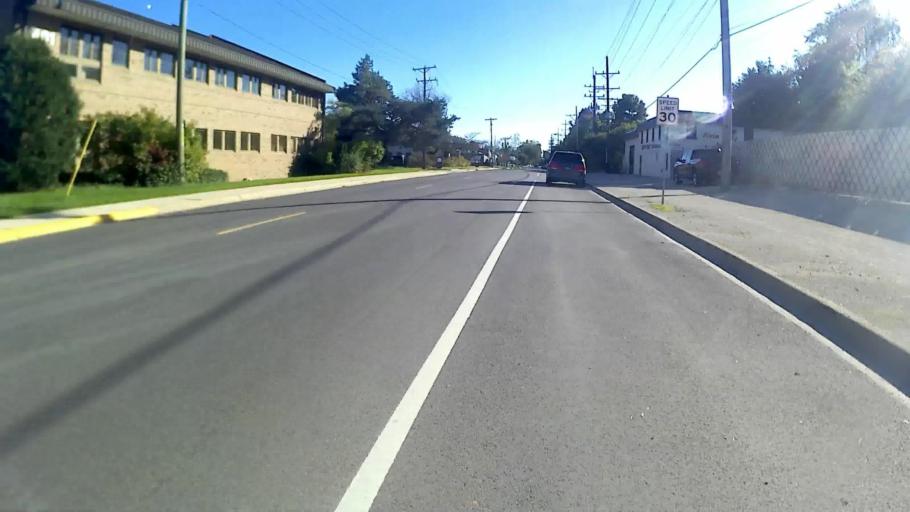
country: US
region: Illinois
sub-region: DuPage County
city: Wheaton
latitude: 41.8622
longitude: -88.1162
